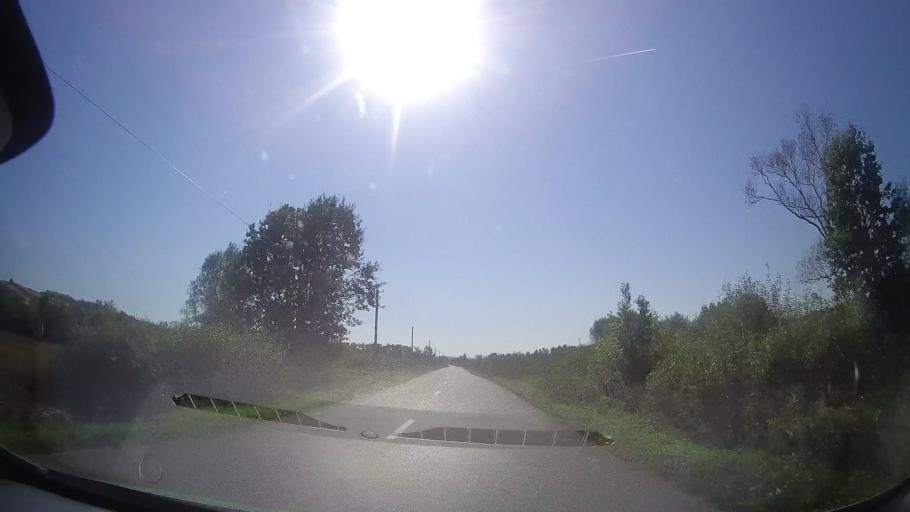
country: RO
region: Timis
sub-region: Comuna Ohaba Lunga
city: Ohaba Lunga
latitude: 45.8792
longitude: 21.9644
